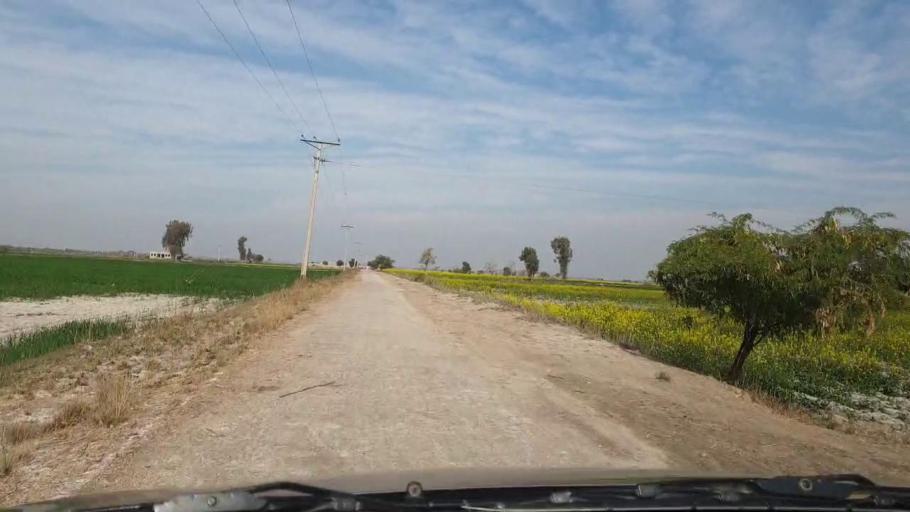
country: PK
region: Sindh
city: Jam Sahib
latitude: 26.2695
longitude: 68.7062
